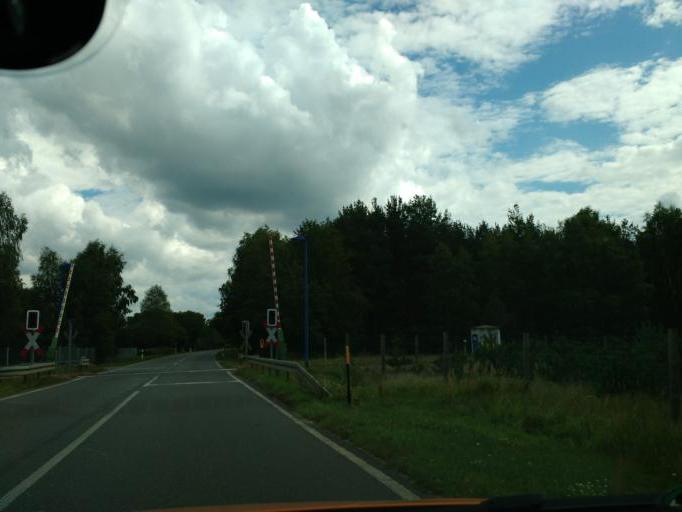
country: DE
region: Brandenburg
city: Marienwerder
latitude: 52.8573
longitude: 13.5466
